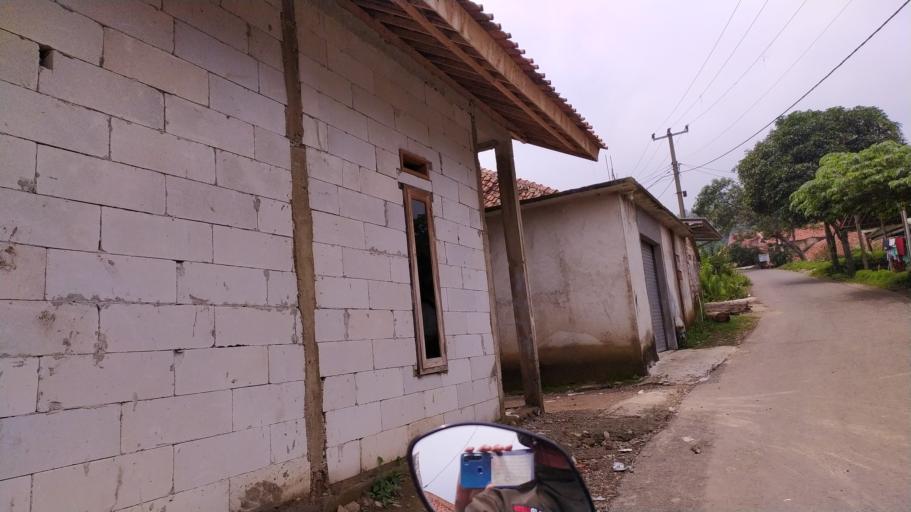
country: ID
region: West Java
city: Ciampea
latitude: -6.6198
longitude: 106.7119
